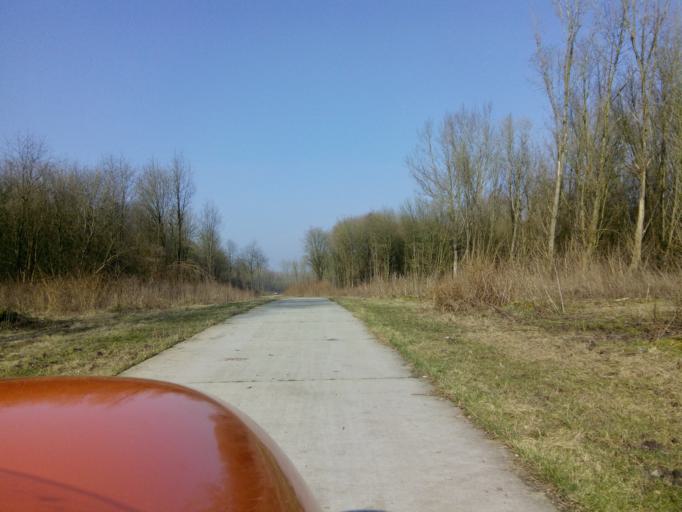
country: NL
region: Gelderland
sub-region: Gemeente Nijkerk
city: Nijkerk
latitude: 52.2910
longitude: 5.4615
